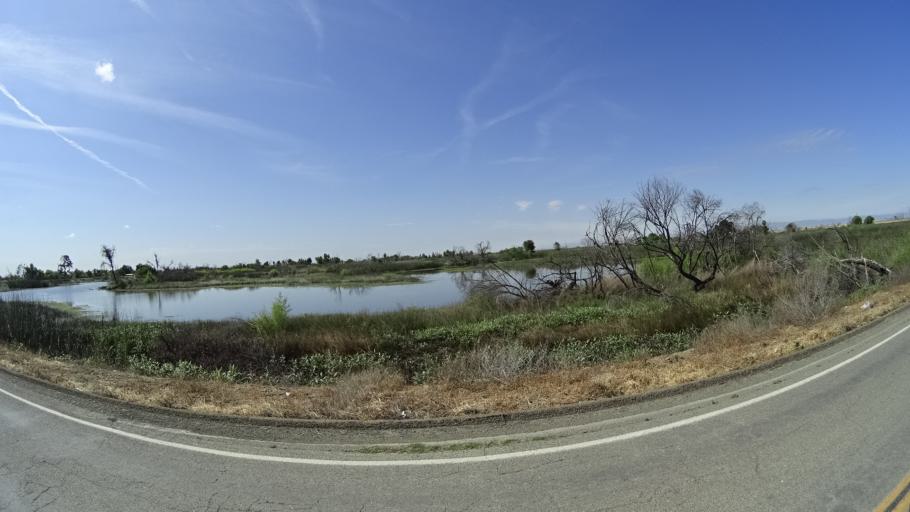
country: US
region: California
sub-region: Kings County
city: Lemoore Station
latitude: 36.2560
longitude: -119.8563
